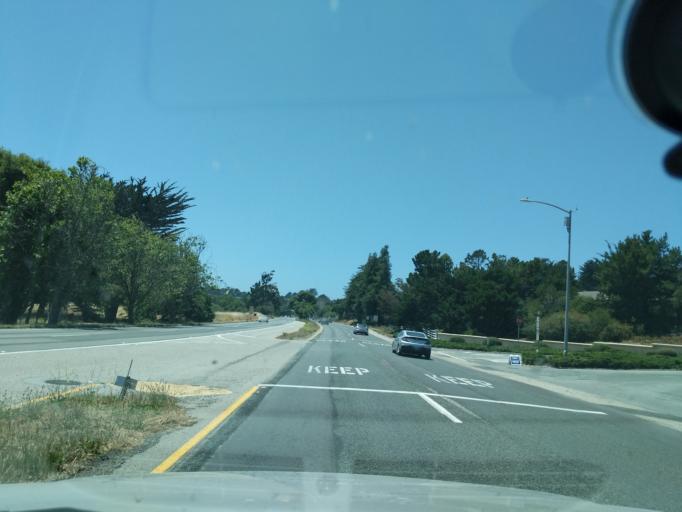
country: US
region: California
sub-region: Monterey County
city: Carmel-by-the-Sea
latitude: 36.5441
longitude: -121.8997
